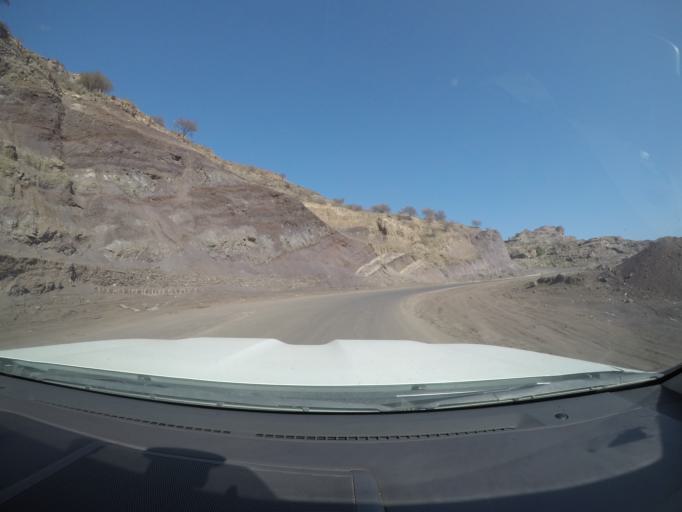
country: YE
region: Ad Dali'
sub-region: Ad Dhale'e
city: Dhalie
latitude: 13.6714
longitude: 44.7663
